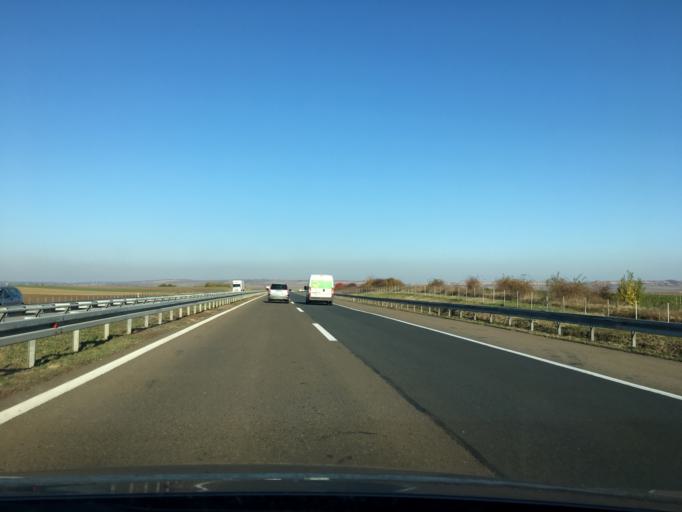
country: RS
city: Beska
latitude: 45.1123
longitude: 20.1021
